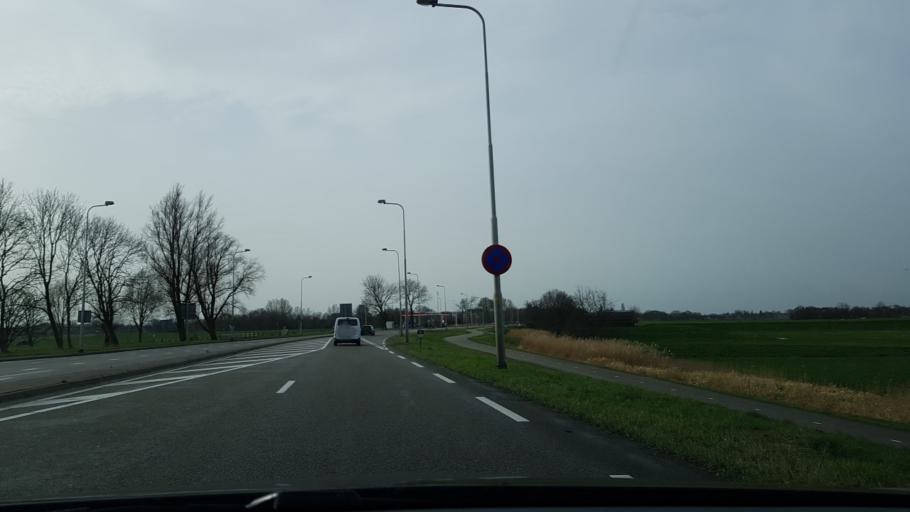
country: NL
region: North Holland
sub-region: Gemeente Ouder-Amstel
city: Ouderkerk aan de Amstel
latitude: 52.3070
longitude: 4.9251
